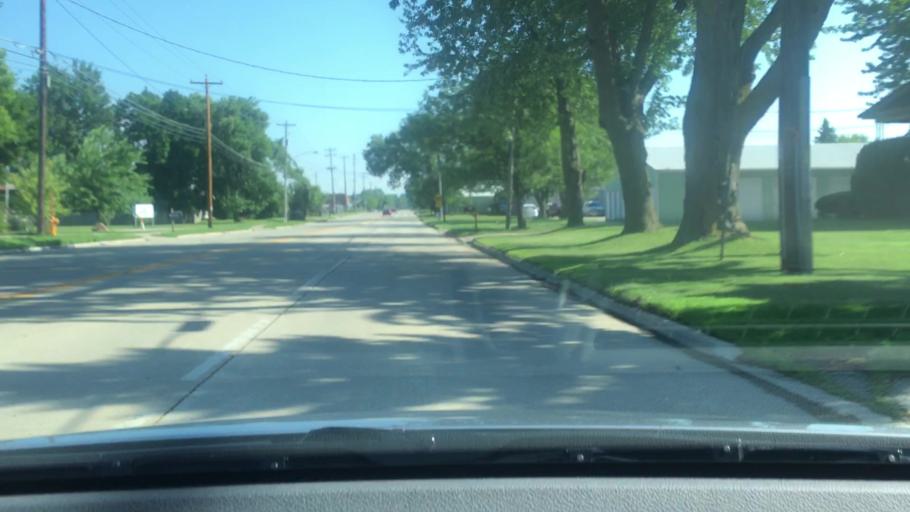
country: US
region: Wisconsin
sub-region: Winnebago County
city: Oshkosh
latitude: 43.9888
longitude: -88.5426
